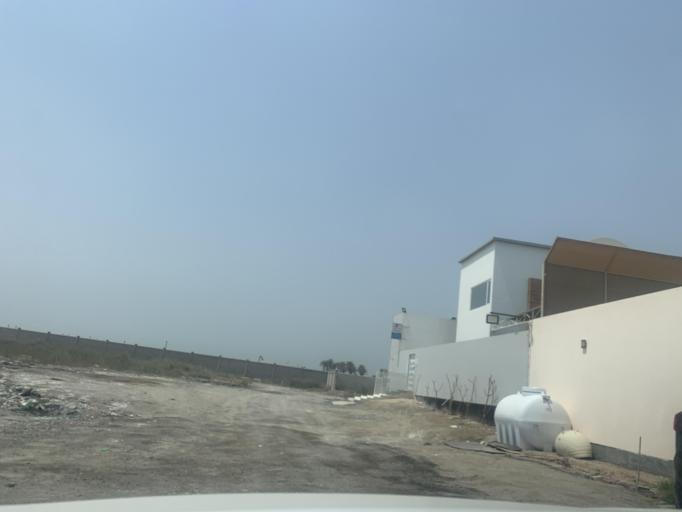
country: BH
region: Central Governorate
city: Madinat Hamad
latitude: 26.1253
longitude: 50.4631
